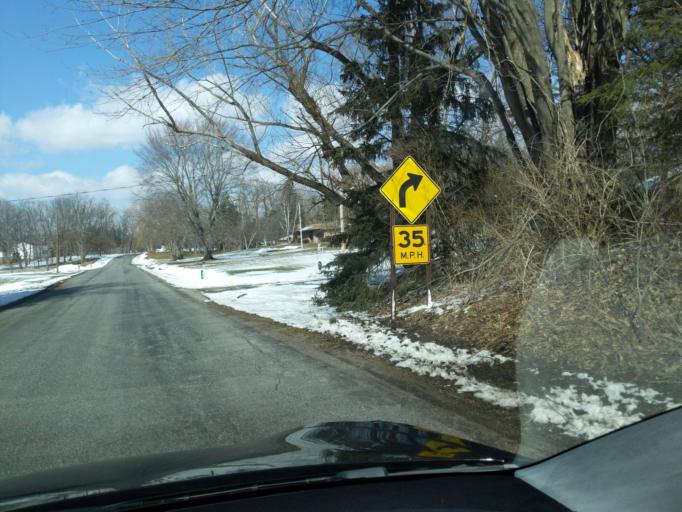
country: US
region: Michigan
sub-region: Ingham County
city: Mason
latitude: 42.6058
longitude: -84.4662
